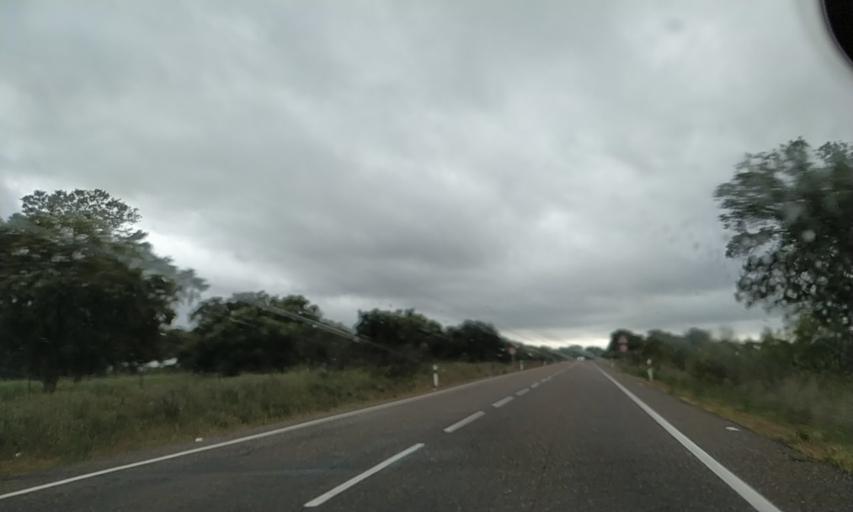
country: ES
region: Extremadura
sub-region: Provincia de Badajoz
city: La Roca de la Sierra
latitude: 39.0825
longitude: -6.7394
